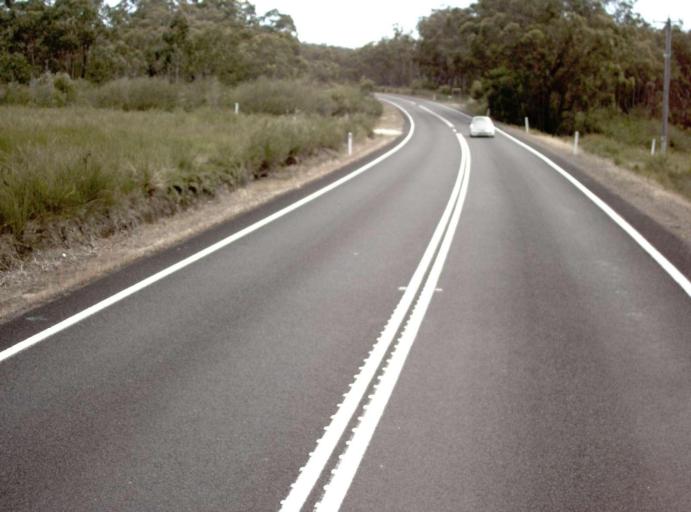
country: AU
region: New South Wales
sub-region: Bega Valley
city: Eden
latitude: -37.4828
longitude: 149.5525
